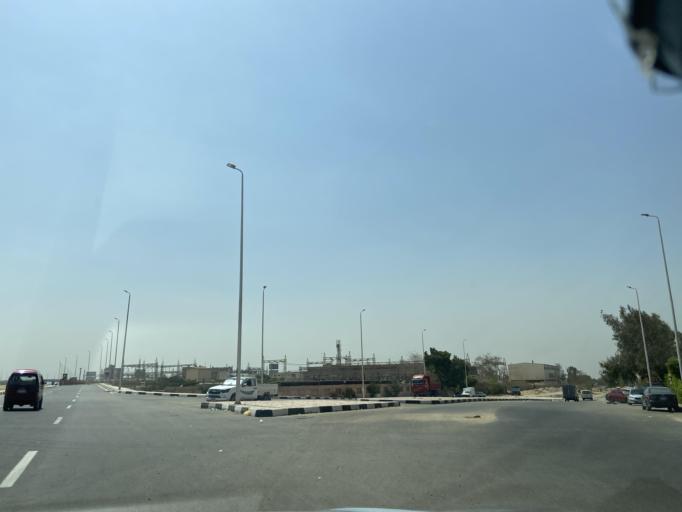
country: EG
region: Muhafazat al Qahirah
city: Cairo
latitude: 30.0437
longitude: 31.3613
